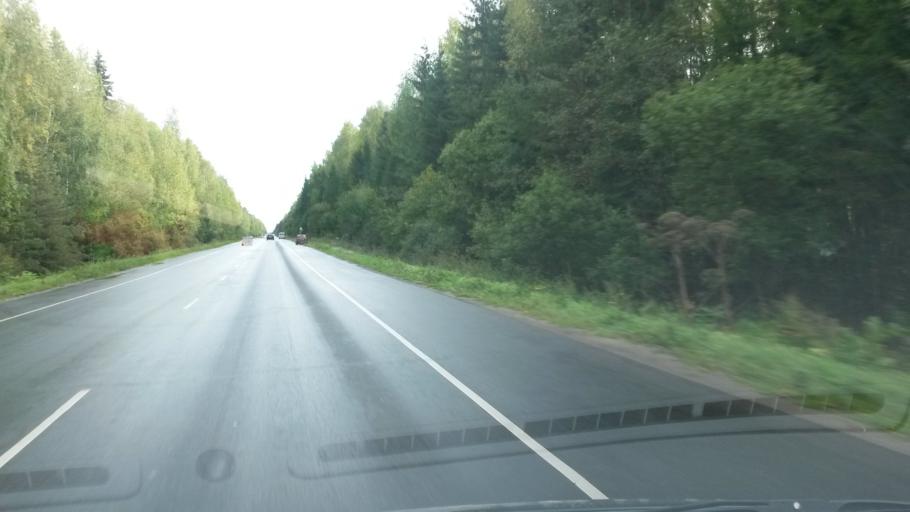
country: RU
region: Ivanovo
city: Kitovo
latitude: 57.0364
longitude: 41.3242
